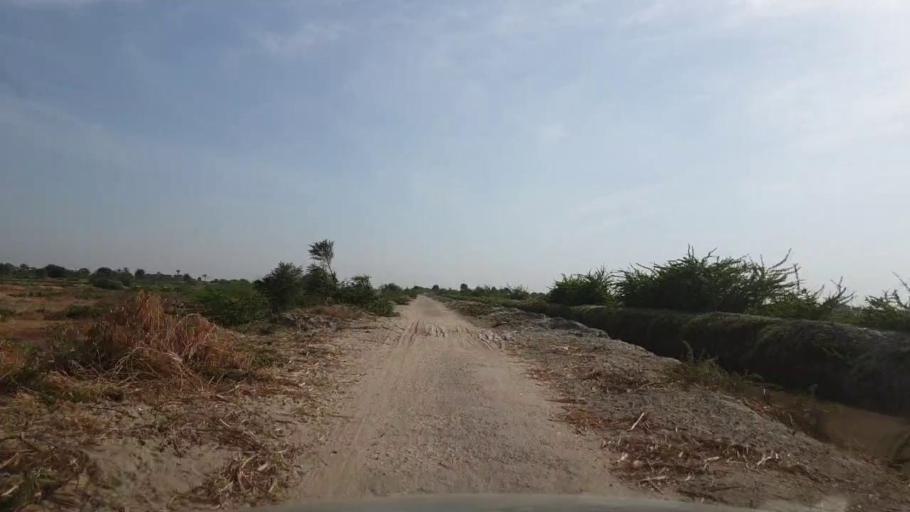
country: PK
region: Sindh
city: Kunri
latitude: 25.1317
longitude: 69.4576
